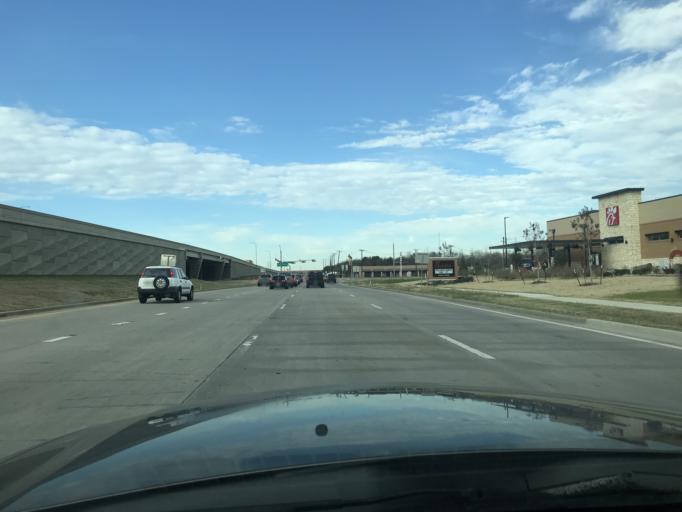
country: US
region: Texas
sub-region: Dallas County
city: Grand Prairie
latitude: 32.7083
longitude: -97.0241
